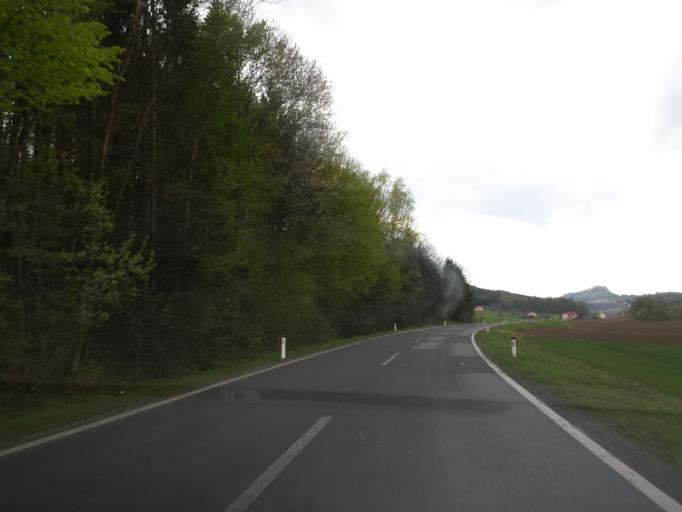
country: AT
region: Styria
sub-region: Politischer Bezirk Suedoststeiermark
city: Hatzendorf
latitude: 46.9856
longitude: 15.9896
